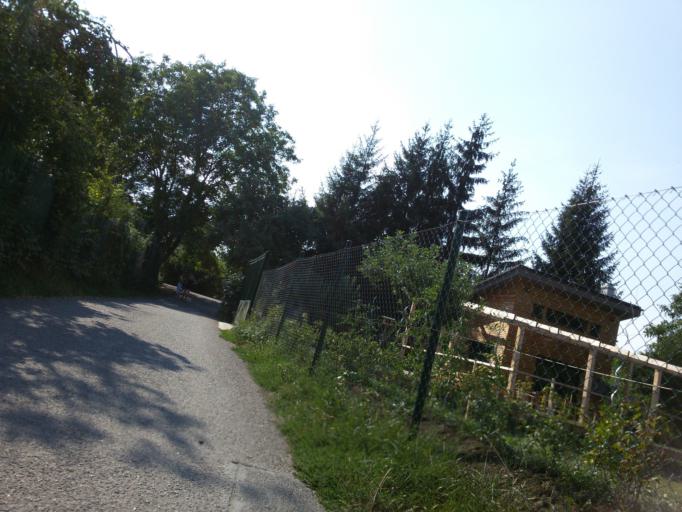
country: CZ
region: South Moravian
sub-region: Mesto Brno
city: Mokra Hora
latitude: 49.2426
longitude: 16.5915
